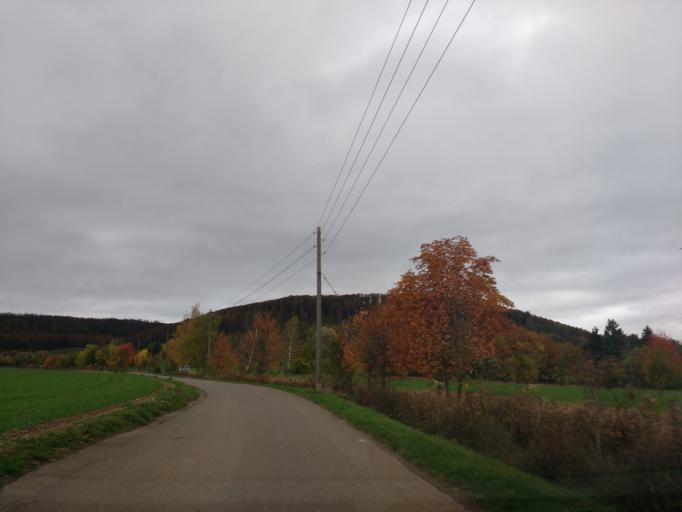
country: DE
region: Thuringia
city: Buhla
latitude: 51.4200
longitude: 10.4257
